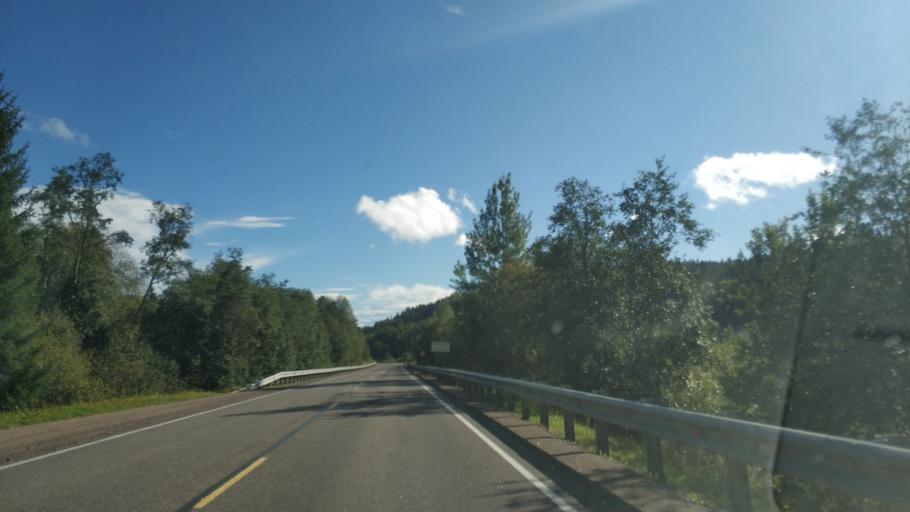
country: RU
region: Republic of Karelia
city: Sortavala
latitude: 61.6702
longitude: 30.6540
